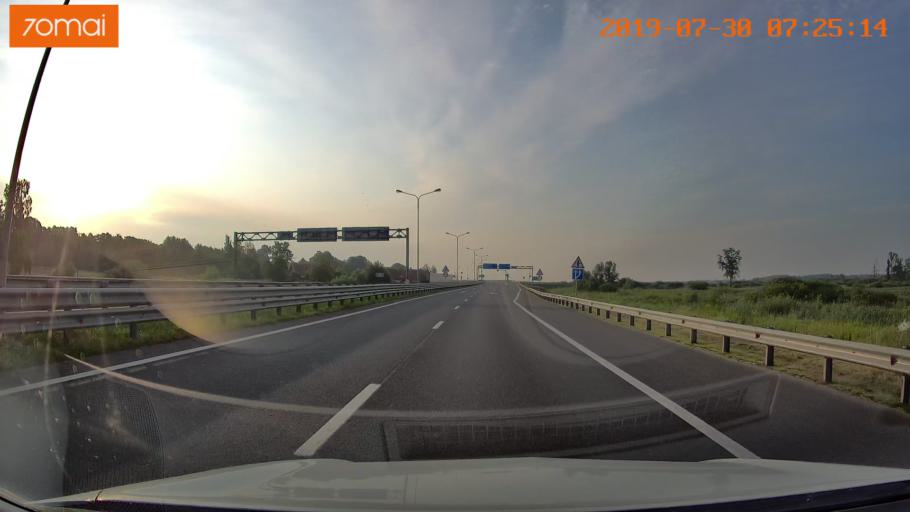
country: RU
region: Kaliningrad
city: Bol'shoe Isakovo
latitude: 54.6880
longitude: 20.8317
